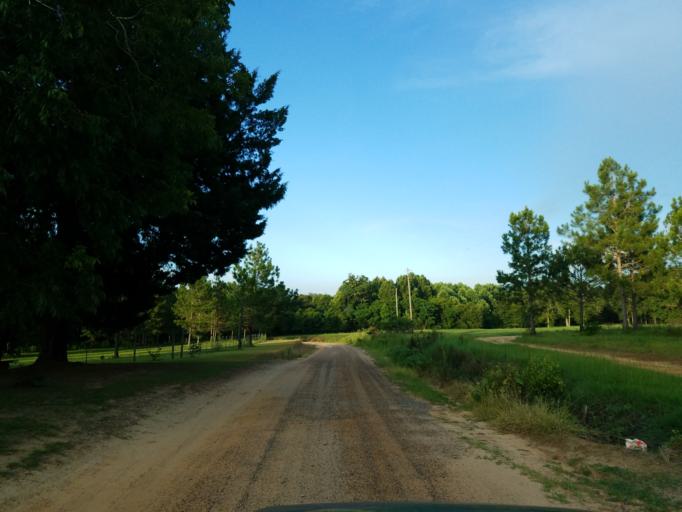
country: US
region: Georgia
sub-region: Turner County
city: Ashburn
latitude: 31.6440
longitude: -83.6044
